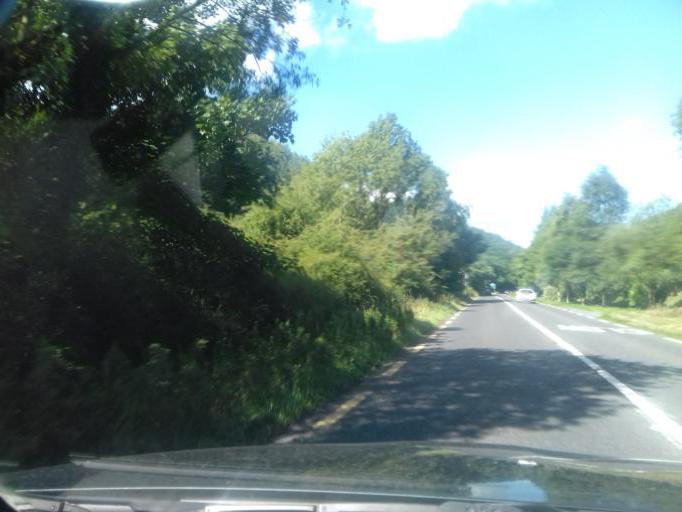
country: IE
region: Munster
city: Carrick-on-Suir
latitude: 52.4080
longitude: -7.4844
